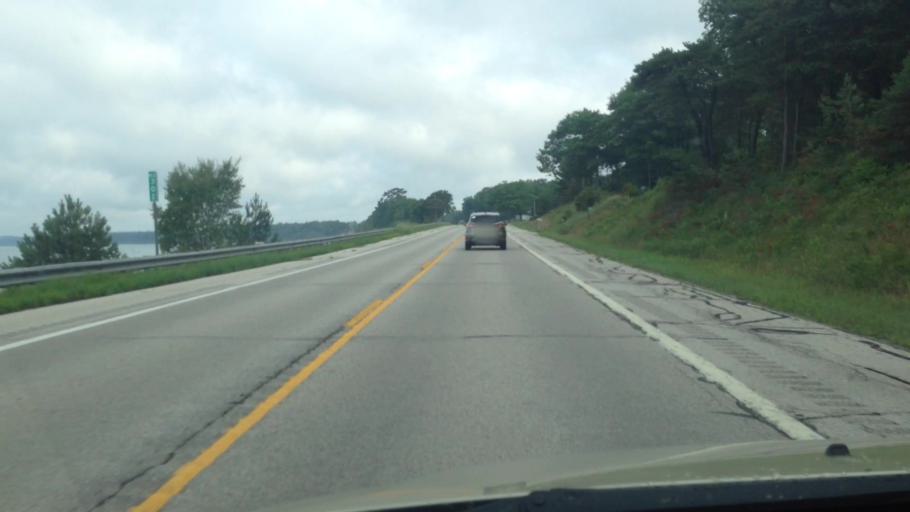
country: US
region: Michigan
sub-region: Mackinac County
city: Saint Ignace
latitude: 45.9991
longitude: -84.9924
